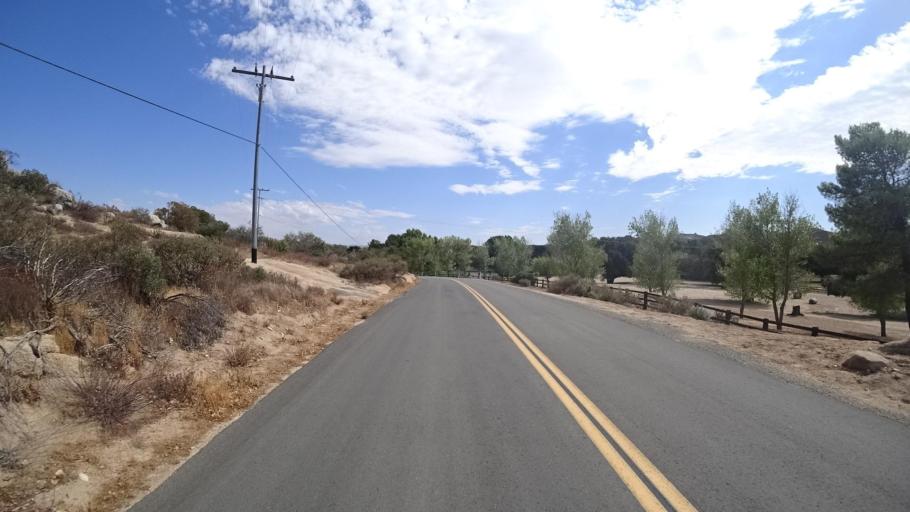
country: MX
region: Baja California
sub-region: Tecate
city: Cereso del Hongo
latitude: 32.6480
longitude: -116.2895
